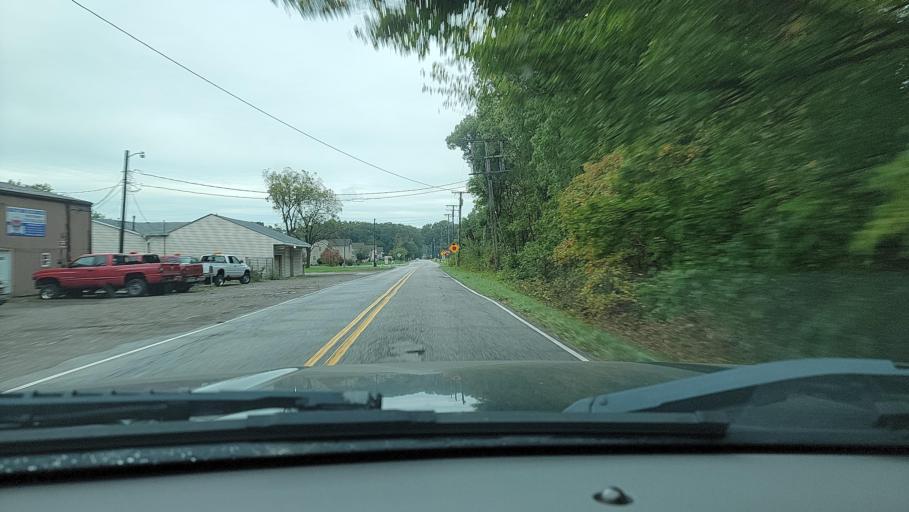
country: US
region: Indiana
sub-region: Porter County
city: Portage
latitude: 41.5748
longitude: -87.1534
